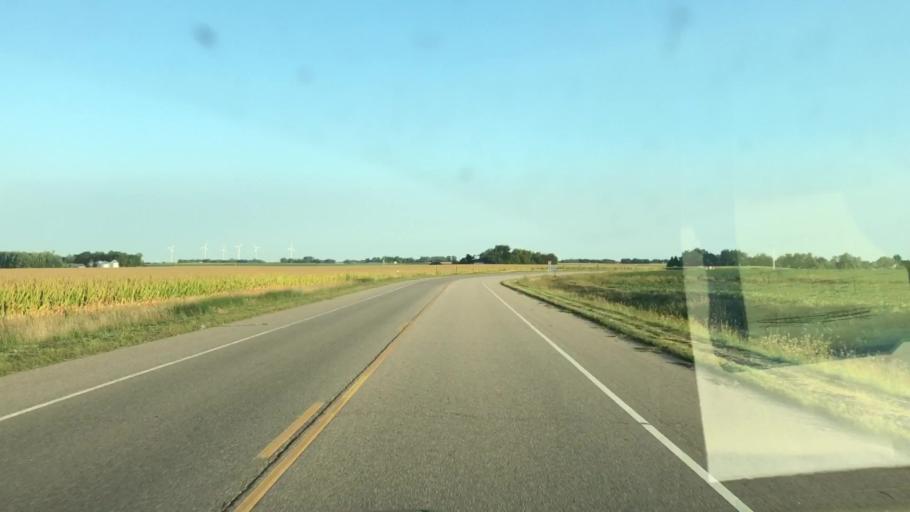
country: US
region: Minnesota
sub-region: Nobles County
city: Worthington
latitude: 43.5987
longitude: -95.6347
